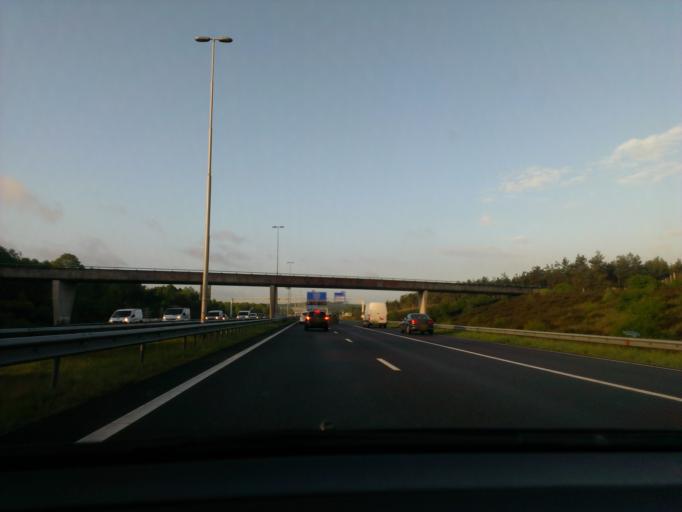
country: NL
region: Gelderland
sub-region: Gemeente Rozendaal
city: Rozendaal
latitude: 52.0335
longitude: 5.9284
